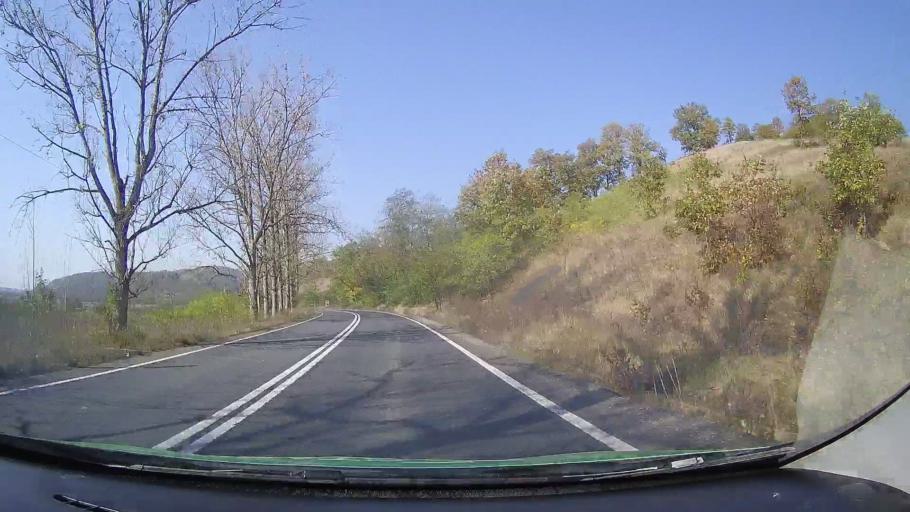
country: RO
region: Arad
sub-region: Comuna Petris
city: Petris
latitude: 46.0062
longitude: 22.3320
